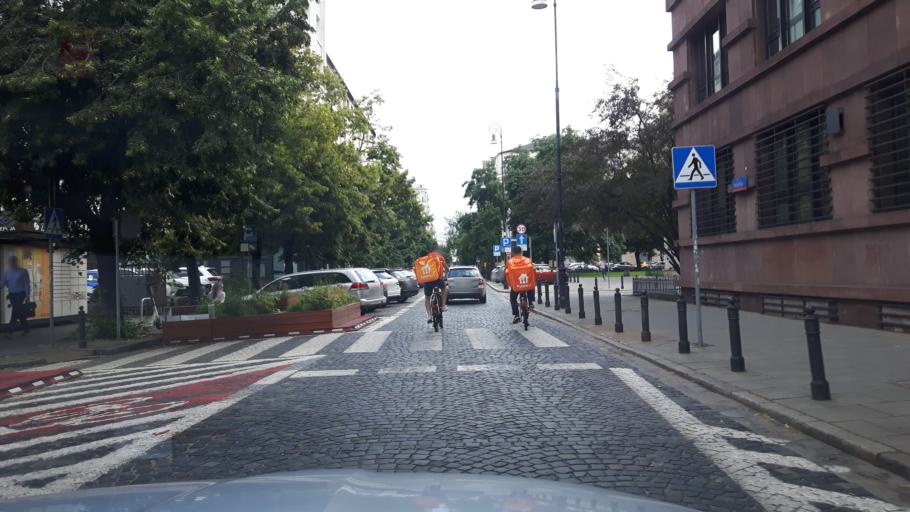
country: PL
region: Masovian Voivodeship
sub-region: Warszawa
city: Warsaw
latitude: 52.2276
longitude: 21.0106
